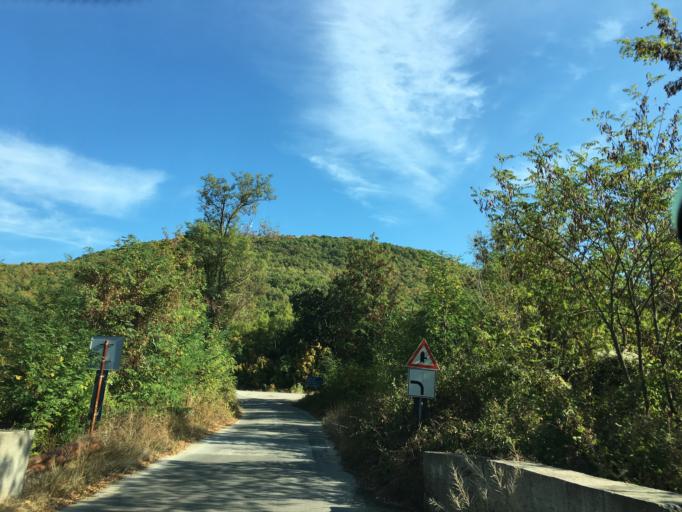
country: BG
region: Khaskovo
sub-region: Obshtina Ivaylovgrad
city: Ivaylovgrad
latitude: 41.4375
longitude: 26.1340
